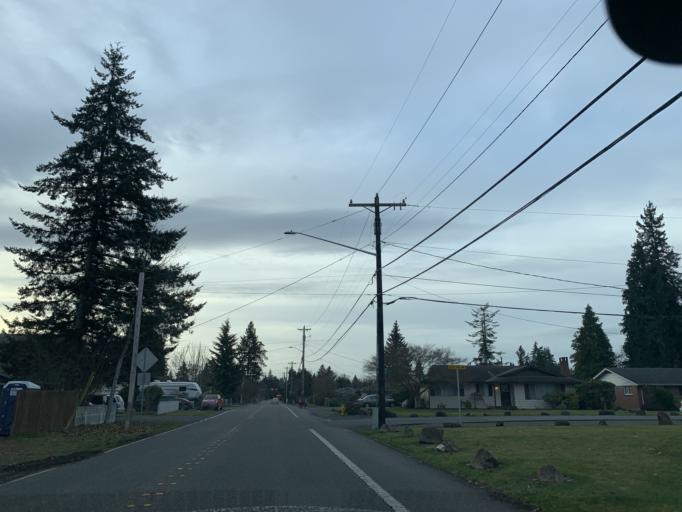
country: US
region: Washington
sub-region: Snohomish County
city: Marysville
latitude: 48.0780
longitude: -122.1564
